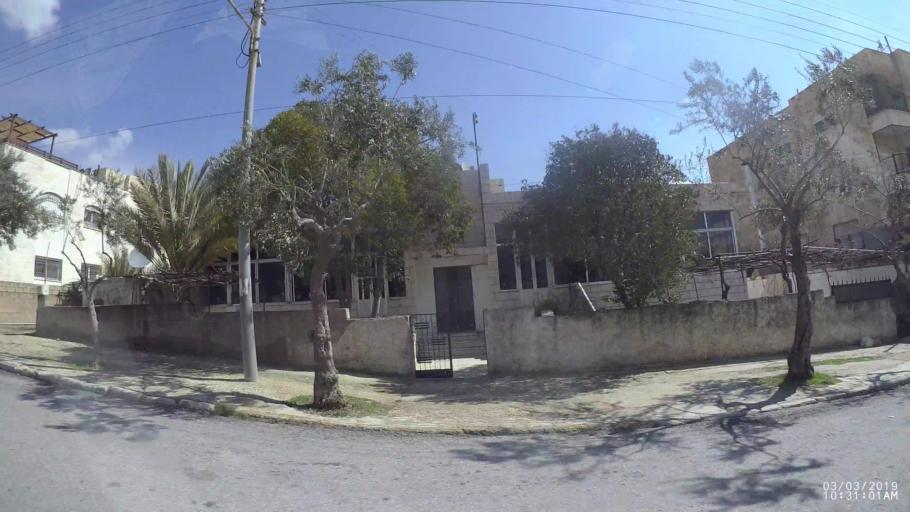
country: JO
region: Amman
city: Al Jubayhah
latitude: 31.9950
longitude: 35.9030
